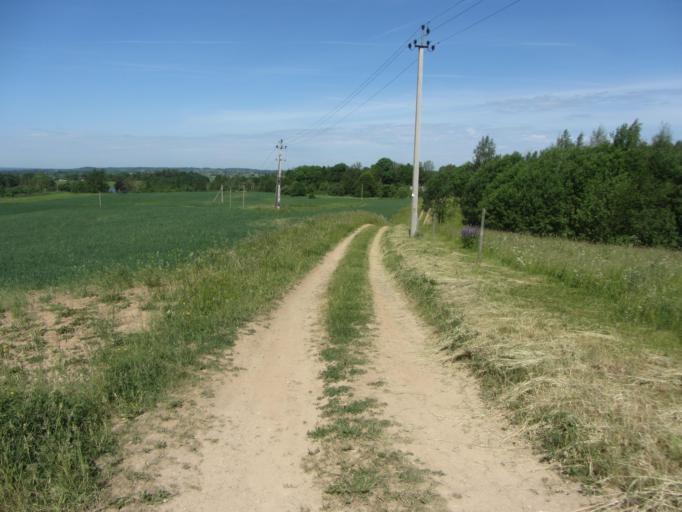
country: LT
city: Ziezmariai
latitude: 54.7190
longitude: 24.3847
